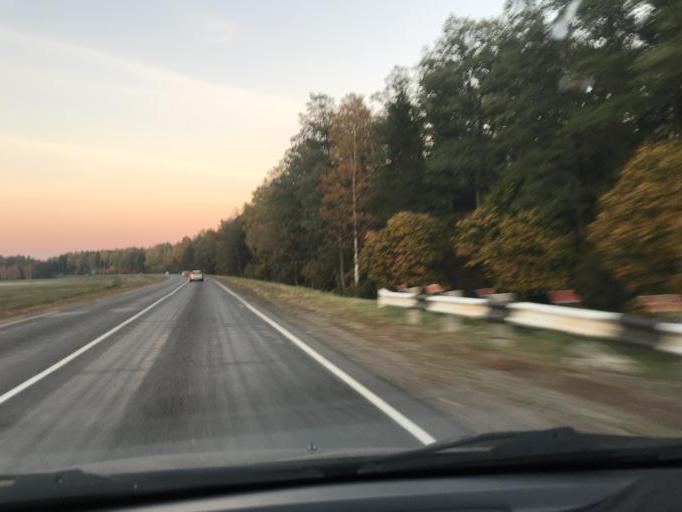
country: BY
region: Mogilev
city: Babruysk
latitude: 53.1986
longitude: 29.0613
